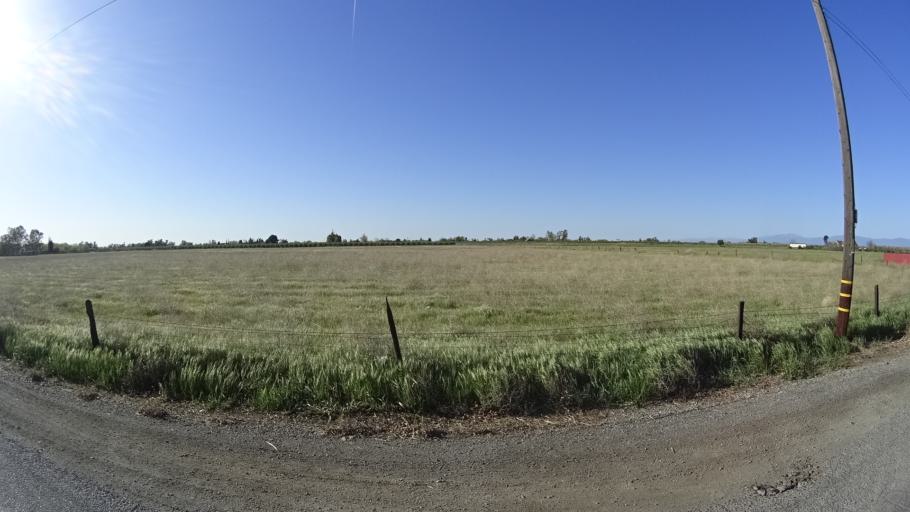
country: US
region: California
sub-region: Glenn County
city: Orland
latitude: 39.7550
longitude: -122.2201
